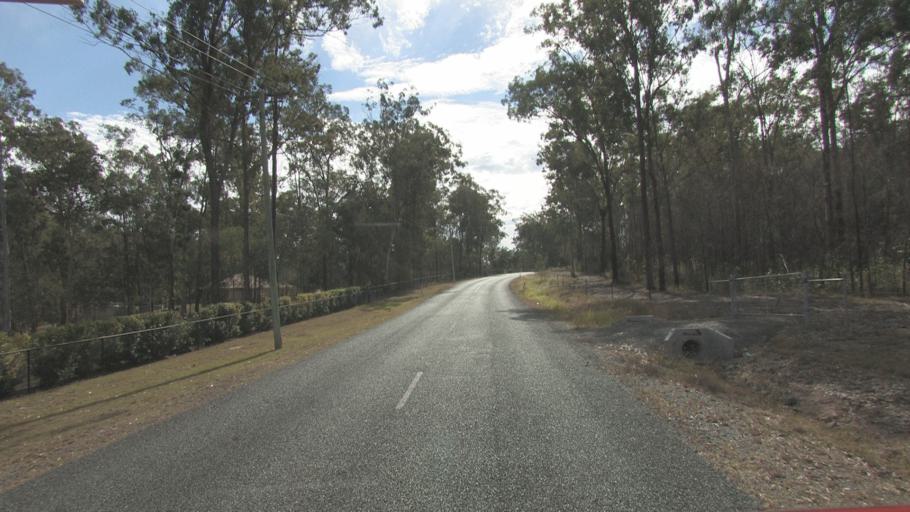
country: AU
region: Queensland
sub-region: Logan
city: North Maclean
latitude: -27.7441
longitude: 152.9734
